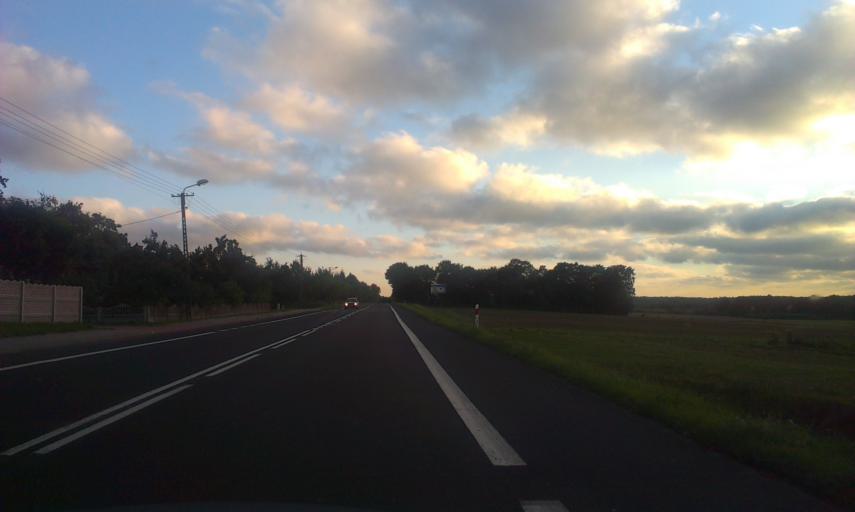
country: PL
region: West Pomeranian Voivodeship
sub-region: Powiat koszalinski
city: Sianow
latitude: 54.2679
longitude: 16.4213
